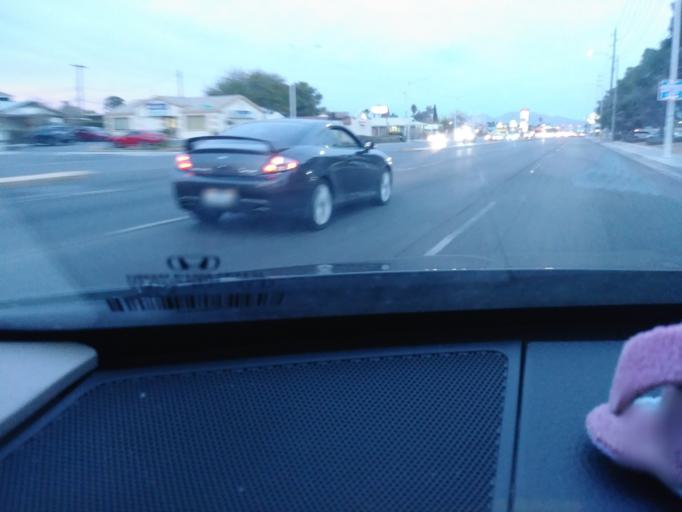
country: US
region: Nevada
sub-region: Clark County
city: Spring Valley
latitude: 36.1591
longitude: -115.2284
